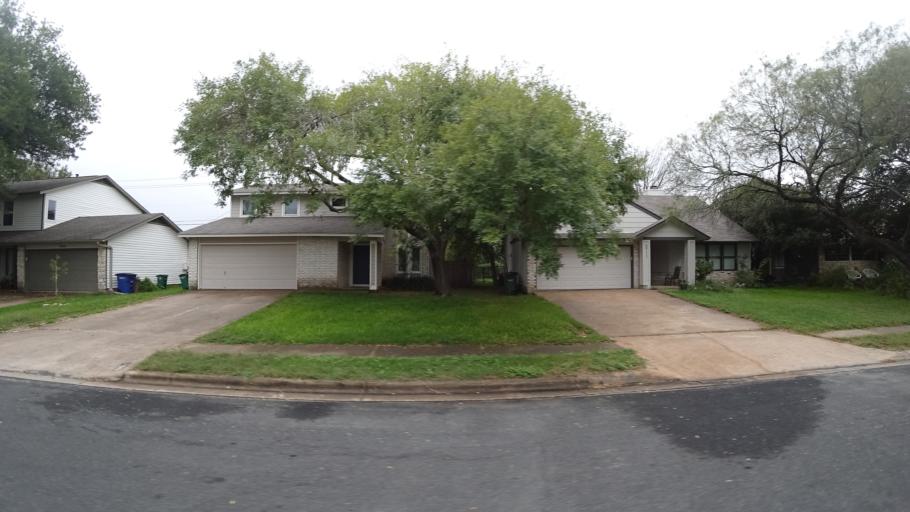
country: US
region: Texas
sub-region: Travis County
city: Shady Hollow
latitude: 30.2010
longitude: -97.8430
